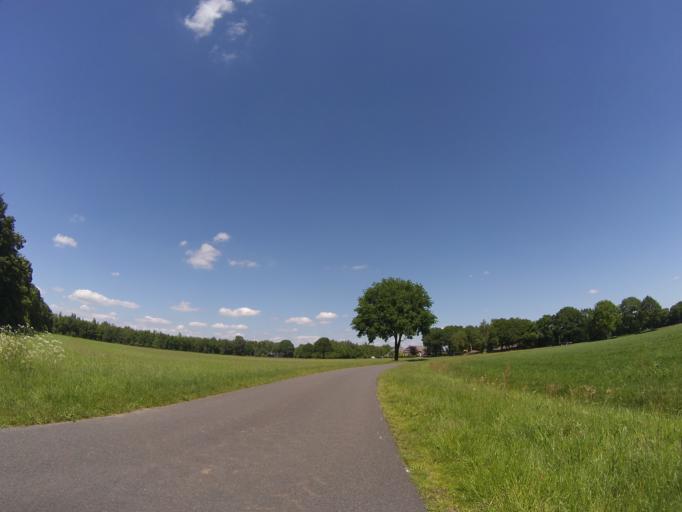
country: NL
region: Drenthe
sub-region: Gemeente Hoogeveen
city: Hoogeveen
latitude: 52.7921
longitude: 6.5326
